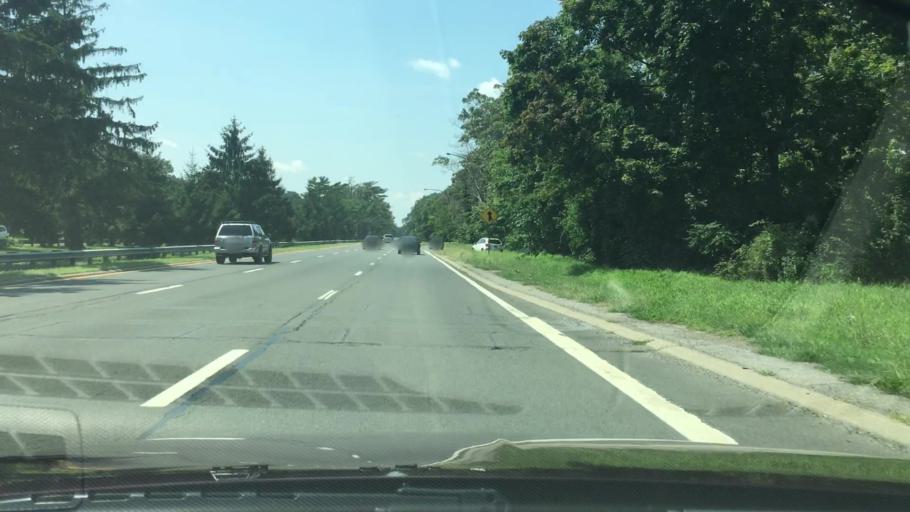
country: US
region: New York
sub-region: Suffolk County
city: West Babylon
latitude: 40.7324
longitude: -73.3473
